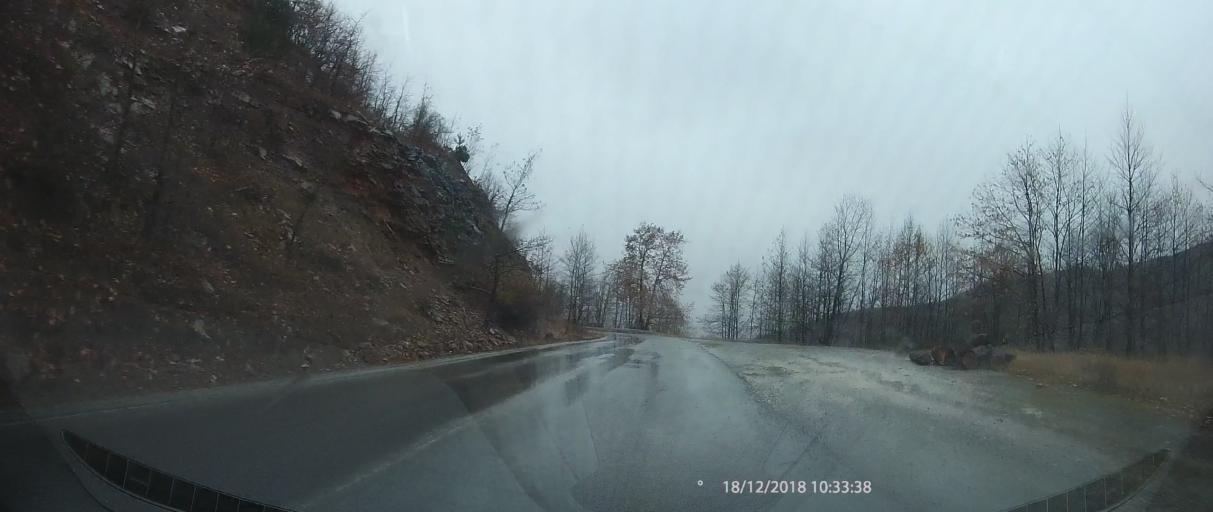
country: GR
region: Central Macedonia
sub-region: Nomos Pierias
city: Kato Milia
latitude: 40.1995
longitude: 22.3001
